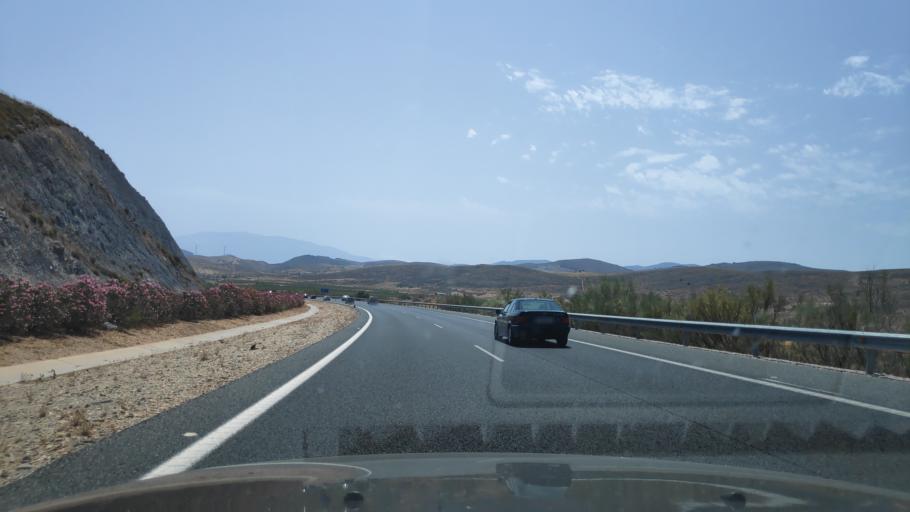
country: ES
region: Andalusia
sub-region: Provincia de Granada
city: Padul
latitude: 36.9942
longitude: -3.6282
